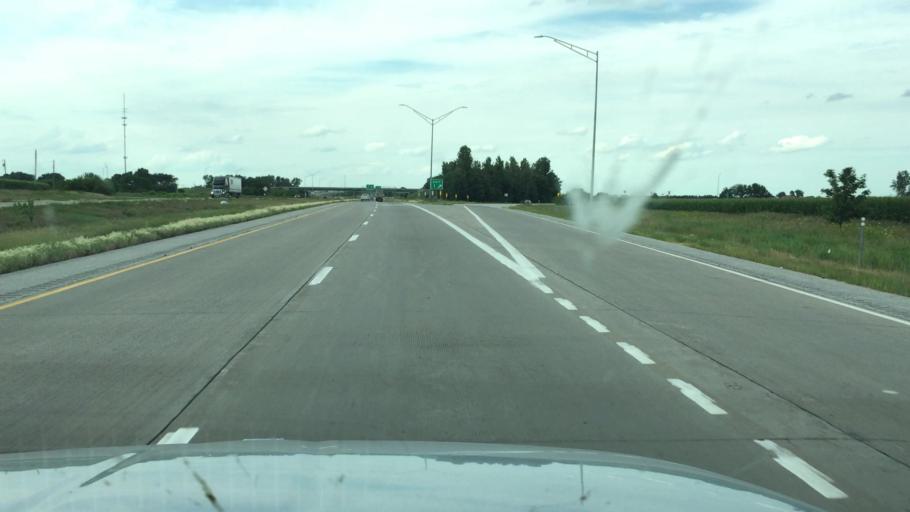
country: US
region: Iowa
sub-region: Scott County
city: Walcott
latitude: 41.5861
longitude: -90.6757
